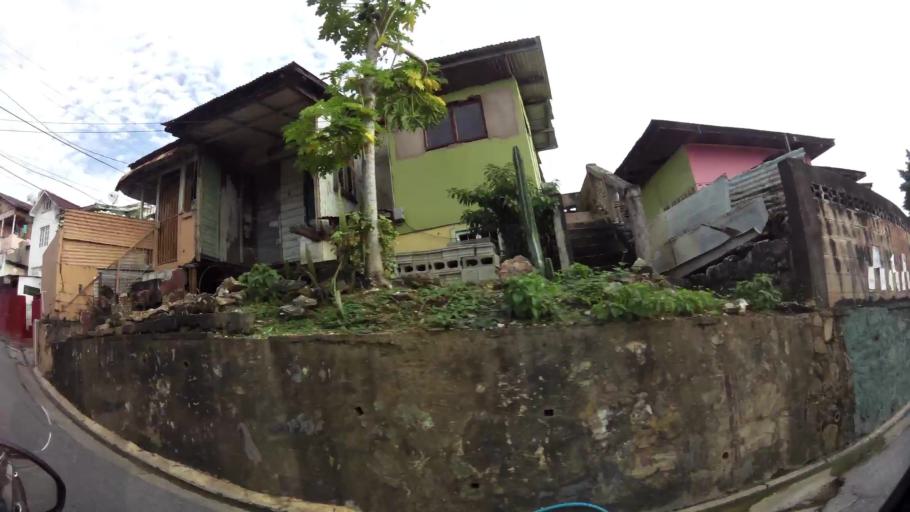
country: TT
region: San Juan/Laventille
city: Laventille
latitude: 10.6560
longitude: -61.4999
